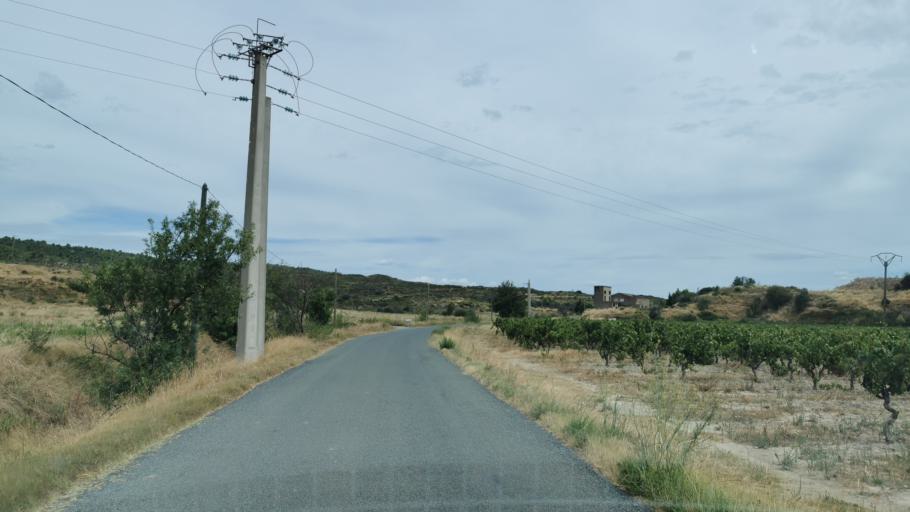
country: FR
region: Languedoc-Roussillon
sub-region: Departement de l'Aude
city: Bize-Minervois
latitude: 43.3065
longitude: 2.8365
